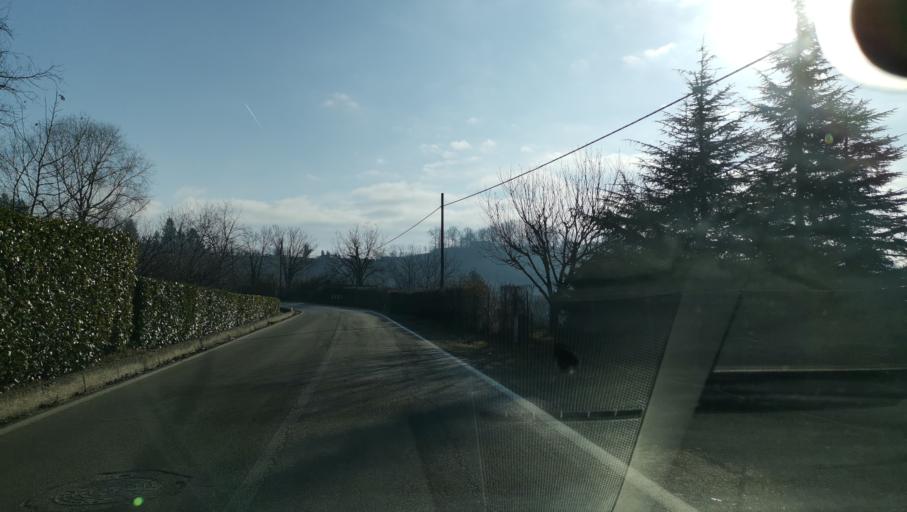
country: IT
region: Piedmont
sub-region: Provincia di Torino
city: Castagneto Po
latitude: 45.1461
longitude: 7.8707
